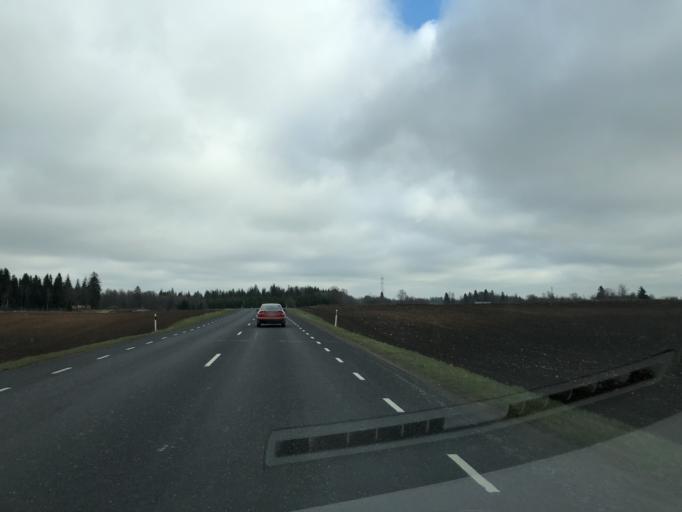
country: EE
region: Laeaene-Virumaa
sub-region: Rakvere linn
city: Rakvere
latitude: 59.2763
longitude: 26.2873
